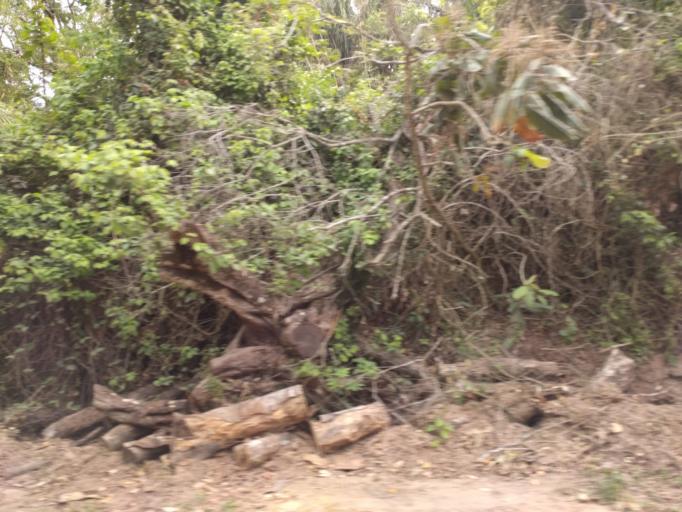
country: BO
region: Santa Cruz
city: Santiago del Torno
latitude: -17.9048
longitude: -63.4367
